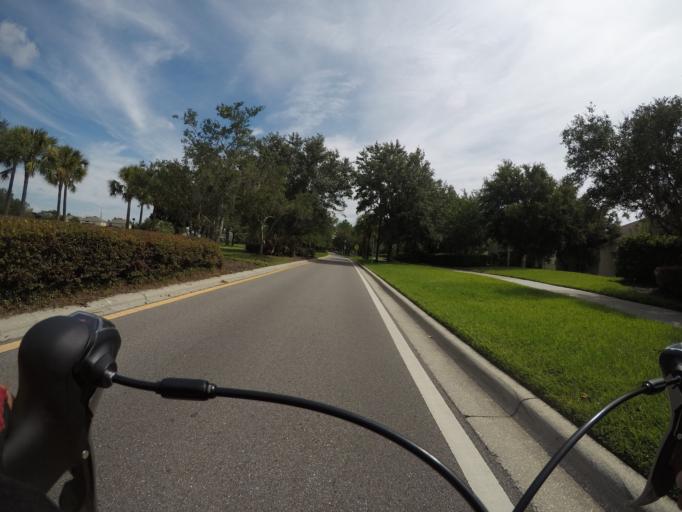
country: US
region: Florida
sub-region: Orange County
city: Conway
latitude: 28.4086
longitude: -81.2202
